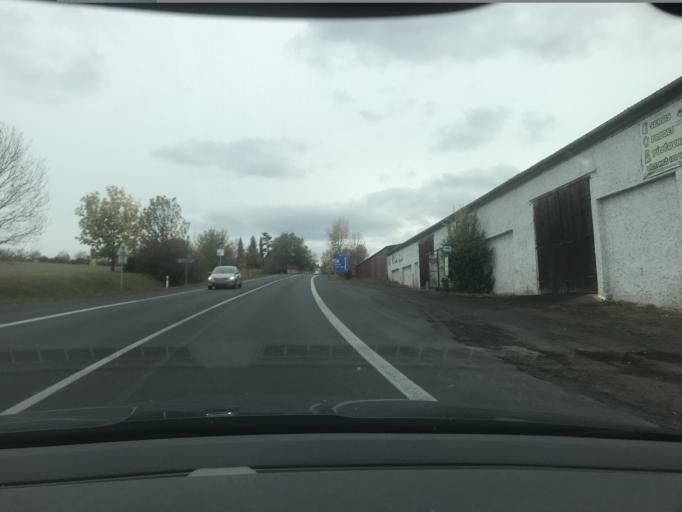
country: CZ
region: Ustecky
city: Trebenice
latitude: 50.4816
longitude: 14.0050
